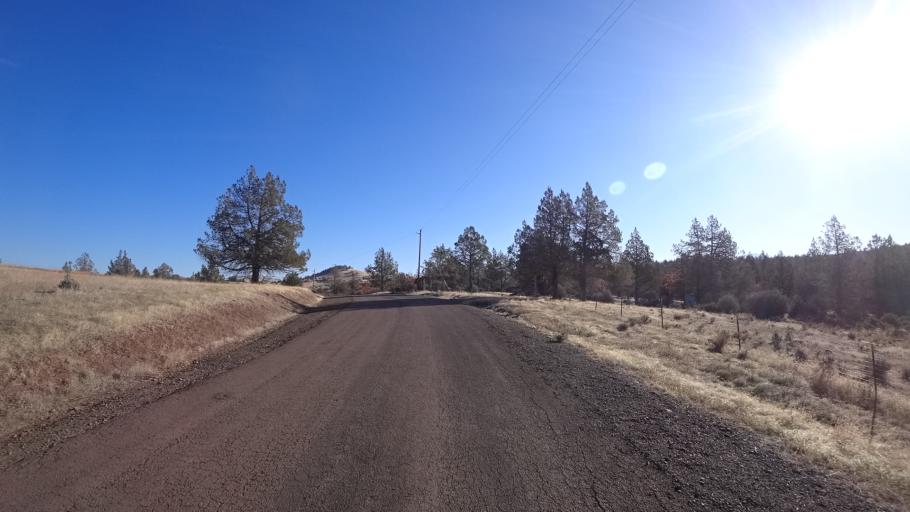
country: US
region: California
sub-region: Siskiyou County
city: Montague
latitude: 41.9130
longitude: -122.4291
